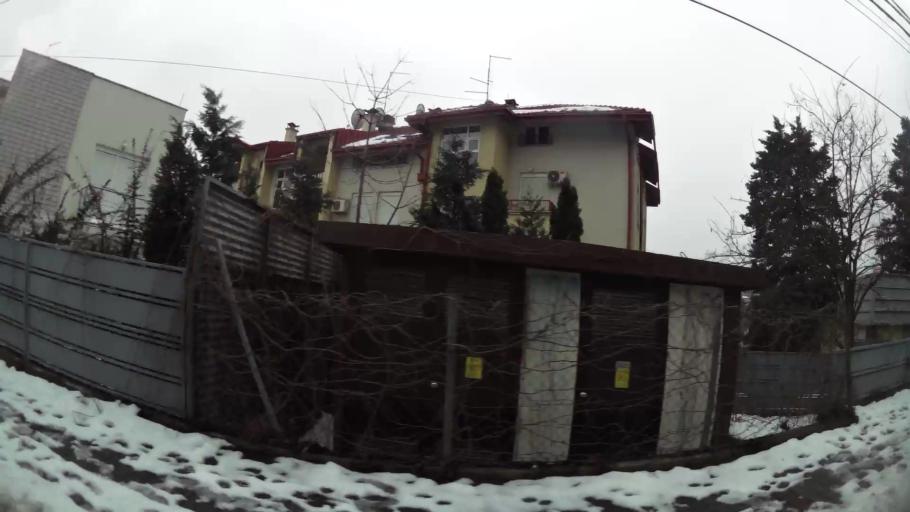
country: RS
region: Central Serbia
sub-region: Belgrade
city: Savski Venac
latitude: 44.7652
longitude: 20.4590
